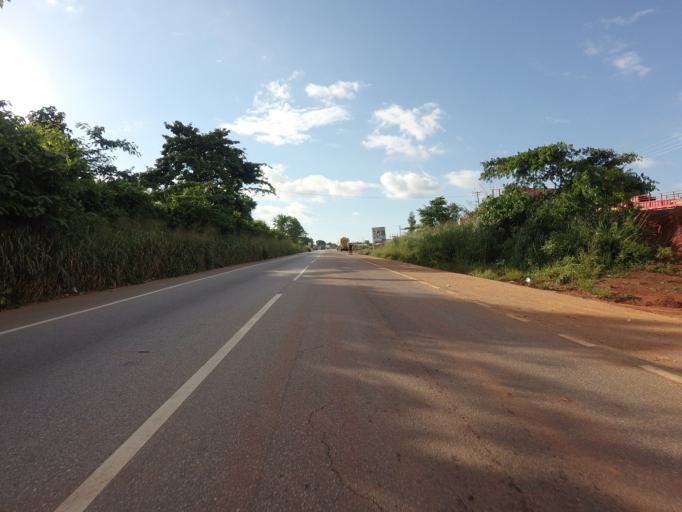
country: GH
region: Ashanti
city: Tafo
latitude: 6.8999
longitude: -1.6540
